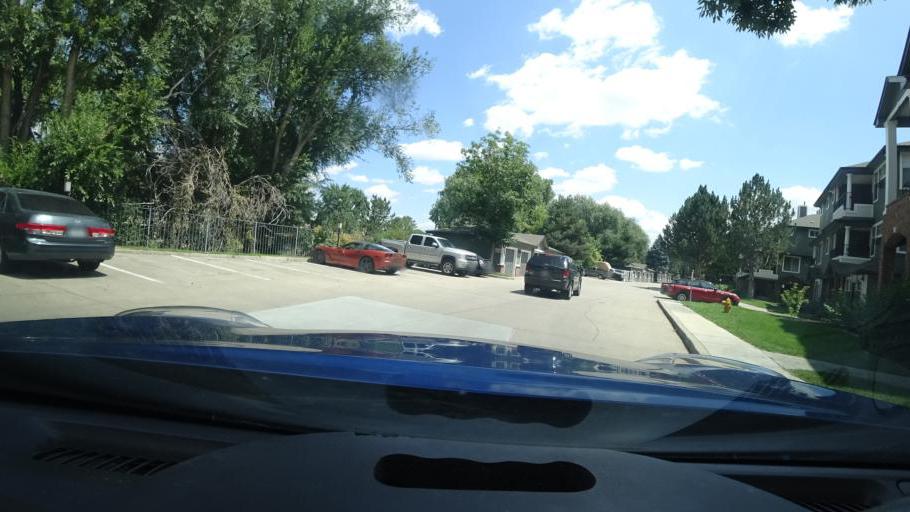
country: US
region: Colorado
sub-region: Adams County
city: Aurora
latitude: 39.7000
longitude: -104.8781
